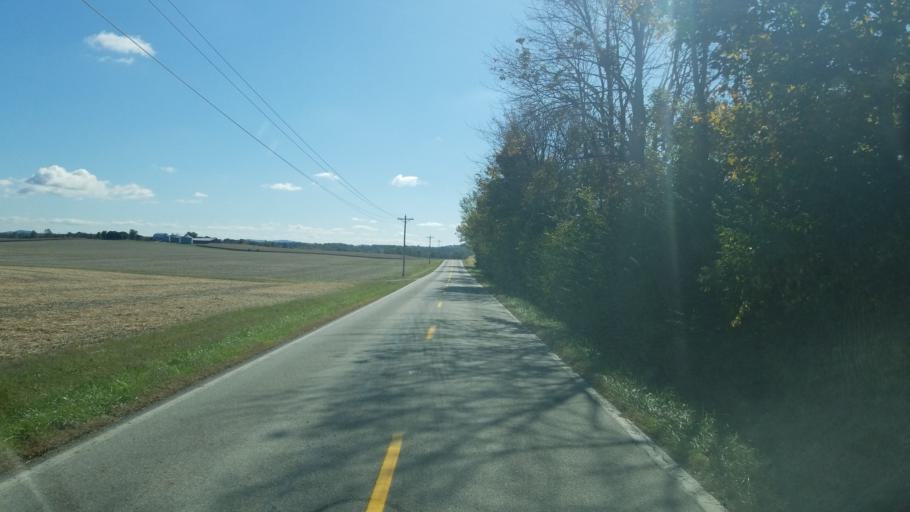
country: US
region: Ohio
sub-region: Highland County
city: Leesburg
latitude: 39.2856
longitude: -83.5012
